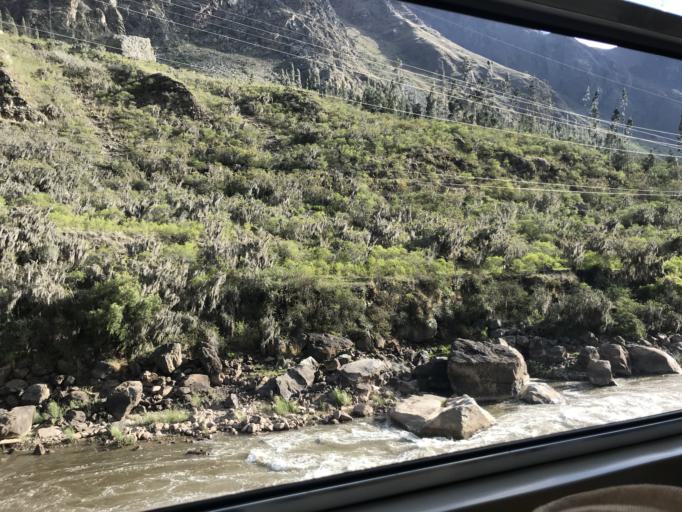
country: PE
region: Cusco
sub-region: Provincia de Urubamba
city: Ollantaytambo
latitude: -13.2264
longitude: -72.3996
